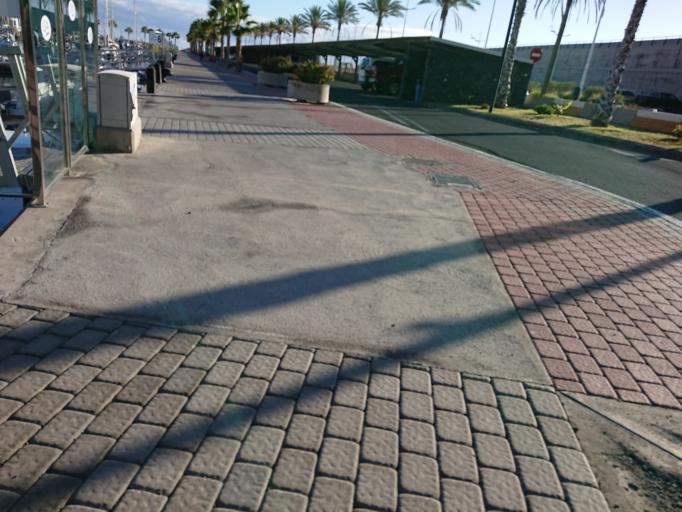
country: ES
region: Canary Islands
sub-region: Provincia de Santa Cruz de Tenerife
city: Tazacorte
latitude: 28.6456
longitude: -17.9444
